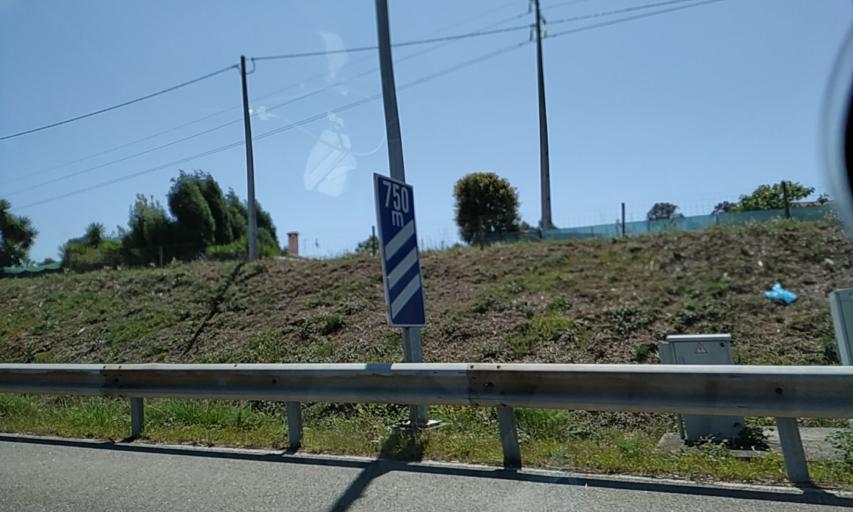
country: PT
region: Aveiro
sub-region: Aveiro
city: Aveiro
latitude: 40.6439
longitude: -8.6085
